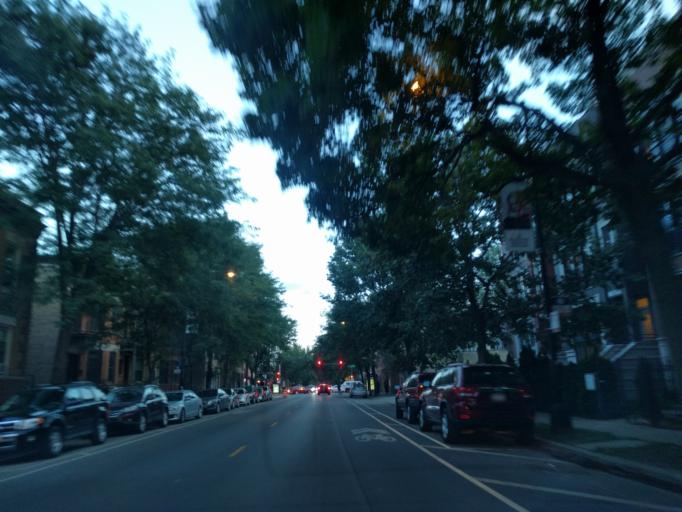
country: US
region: Illinois
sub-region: Cook County
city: Lincolnwood
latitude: 41.9478
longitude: -87.6786
